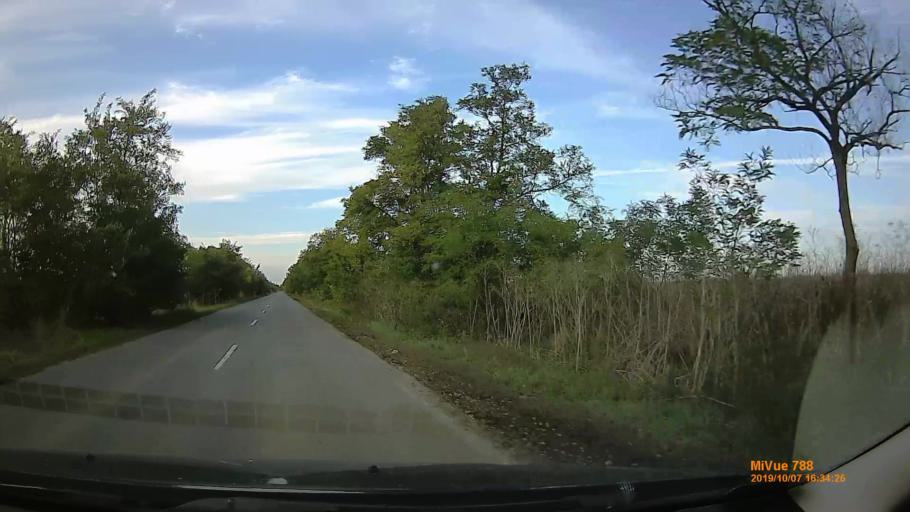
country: HU
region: Bekes
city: Szarvas
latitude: 46.8009
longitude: 20.6206
